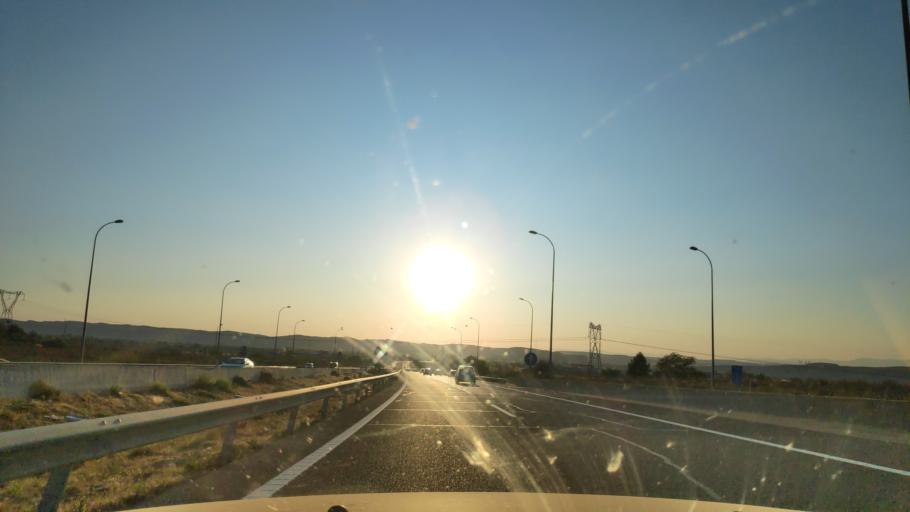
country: ES
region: Madrid
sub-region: Provincia de Madrid
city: Arganda
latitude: 40.2958
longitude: -3.4668
